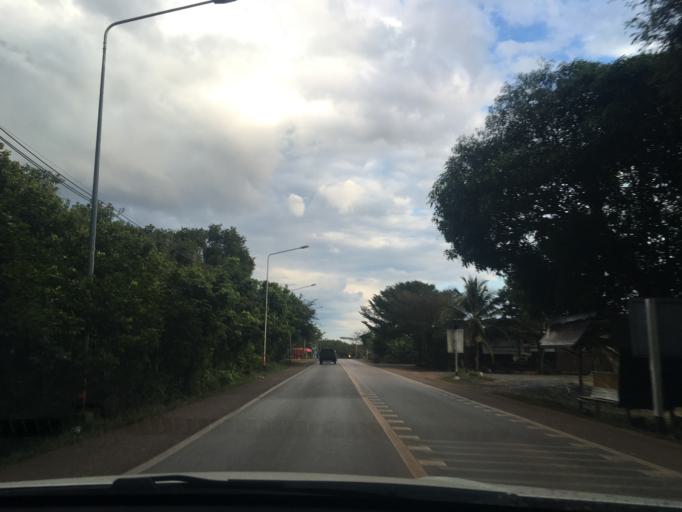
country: TH
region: Rayong
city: Klaeng
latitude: 12.7469
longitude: 101.7327
